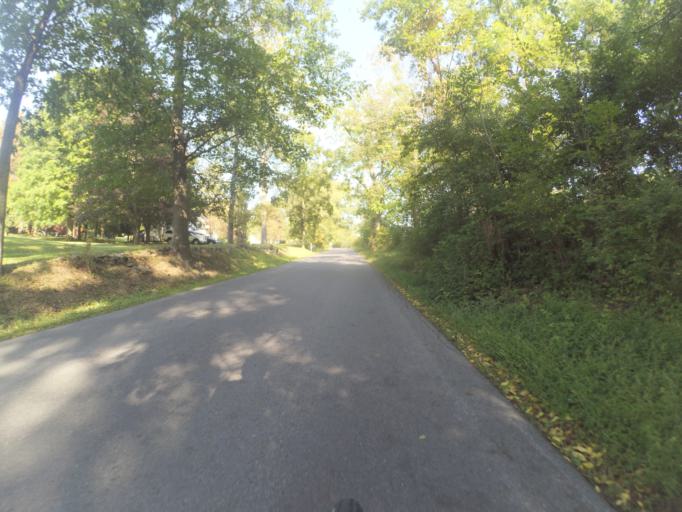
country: US
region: Pennsylvania
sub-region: Centre County
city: Boalsburg
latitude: 40.7991
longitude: -77.7855
